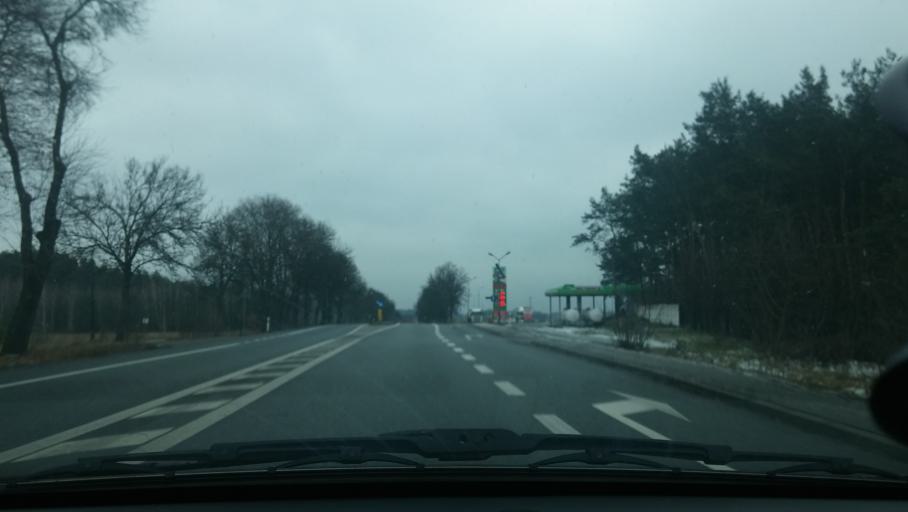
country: PL
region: Masovian Voivodeship
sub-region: Powiat siedlecki
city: Kotun
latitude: 52.1963
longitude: 22.0458
